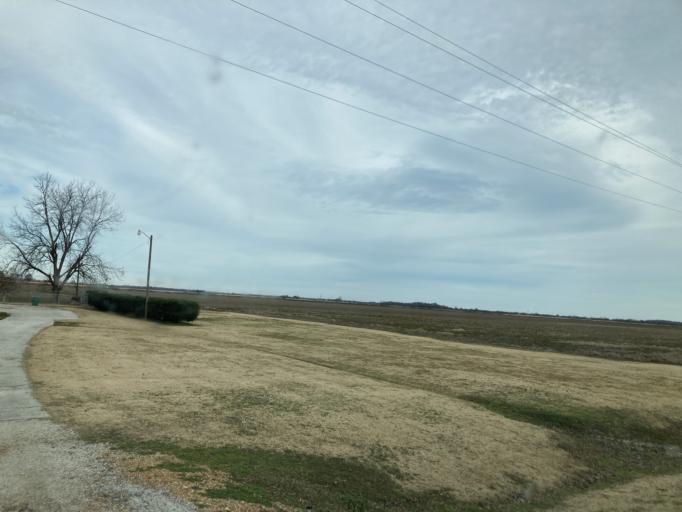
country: US
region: Mississippi
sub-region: Washington County
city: Hollandale
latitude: 33.1845
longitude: -90.6806
